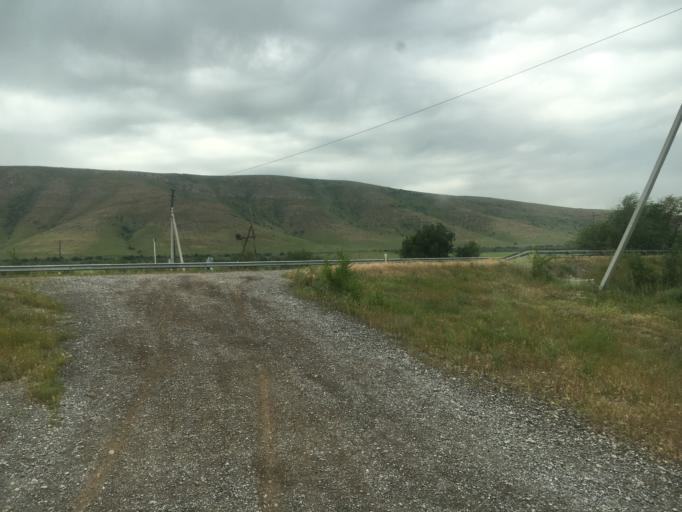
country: KZ
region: Ongtustik Qazaqstan
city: Sastobe
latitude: 42.5502
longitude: 70.0977
